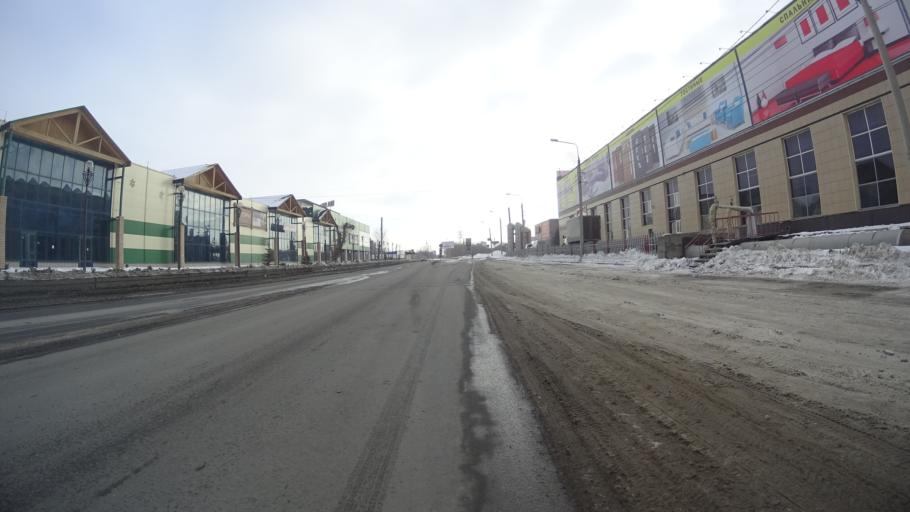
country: RU
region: Chelyabinsk
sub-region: Gorod Chelyabinsk
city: Chelyabinsk
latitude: 55.1196
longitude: 61.3861
